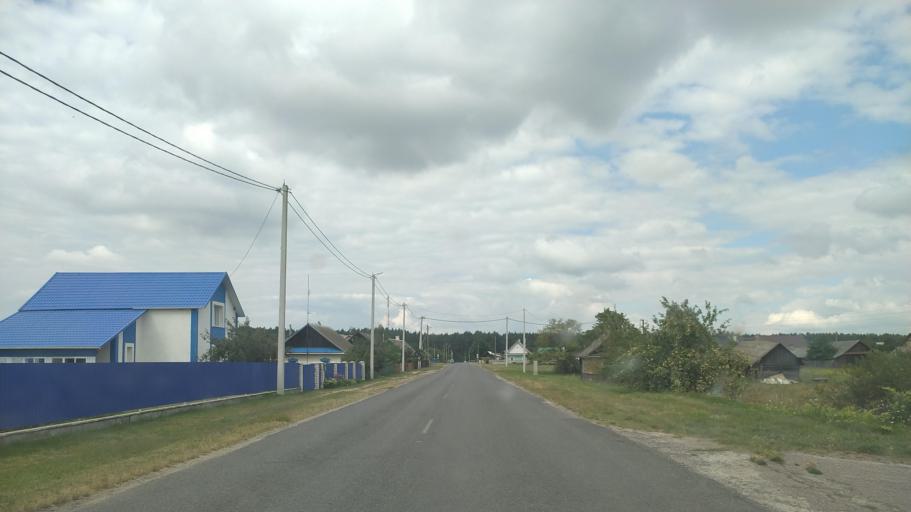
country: BY
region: Brest
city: Byaroza
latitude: 52.5432
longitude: 25.0681
